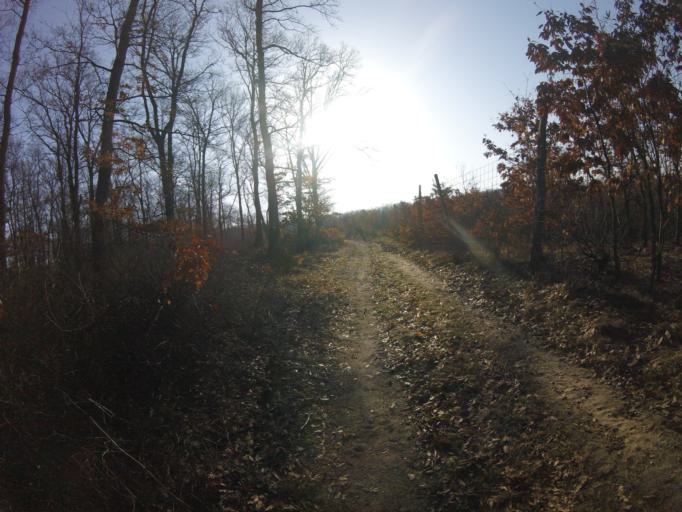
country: HU
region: Komarom-Esztergom
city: Oroszlany
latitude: 47.4890
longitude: 18.3524
